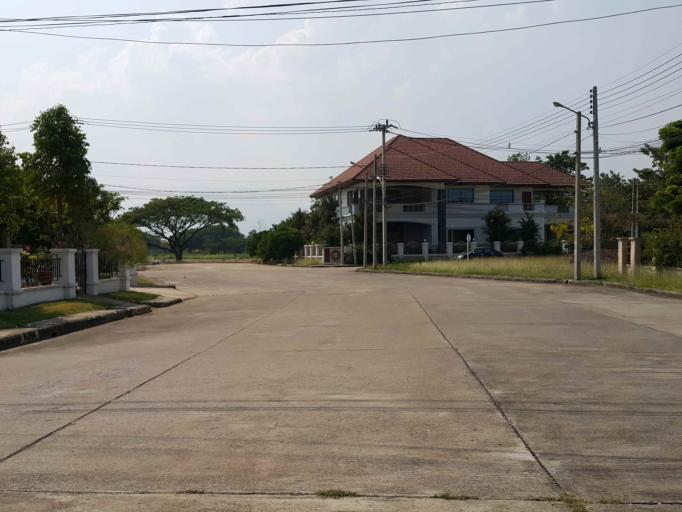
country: TH
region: Chiang Mai
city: Saraphi
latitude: 18.7558
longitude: 99.0461
